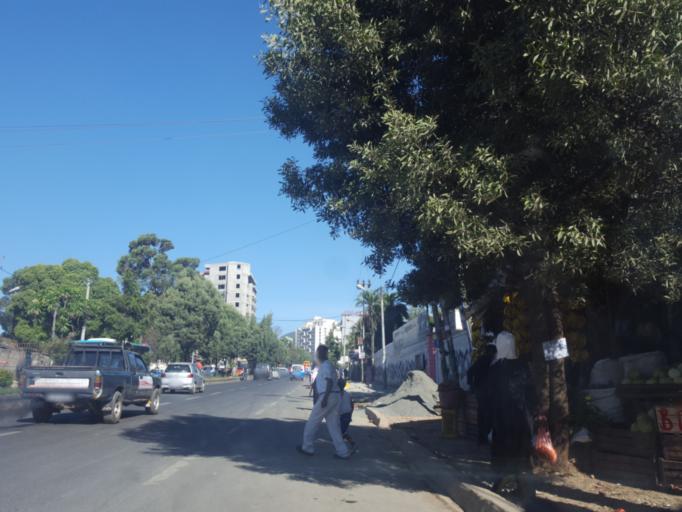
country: ET
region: Adis Abeba
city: Addis Ababa
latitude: 9.0533
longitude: 38.7430
